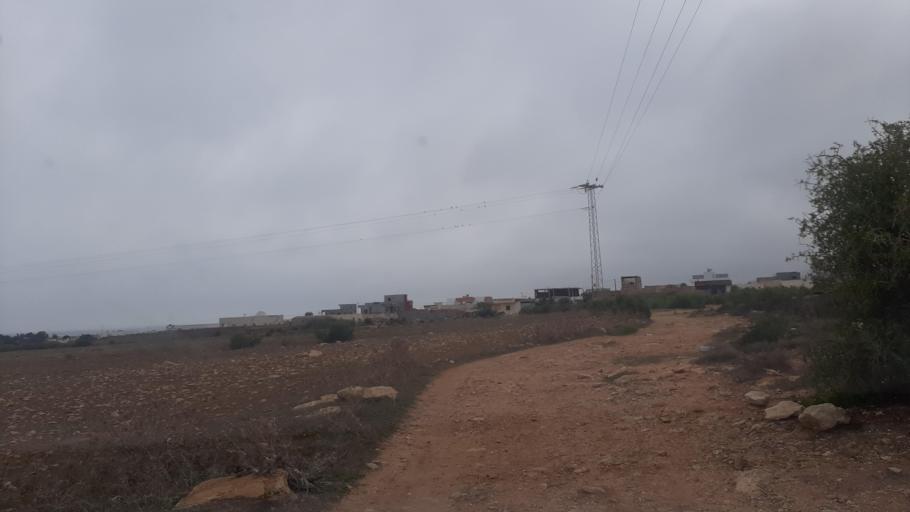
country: TN
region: Nabul
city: Menzel Heurr
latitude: 36.6862
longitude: 10.9307
